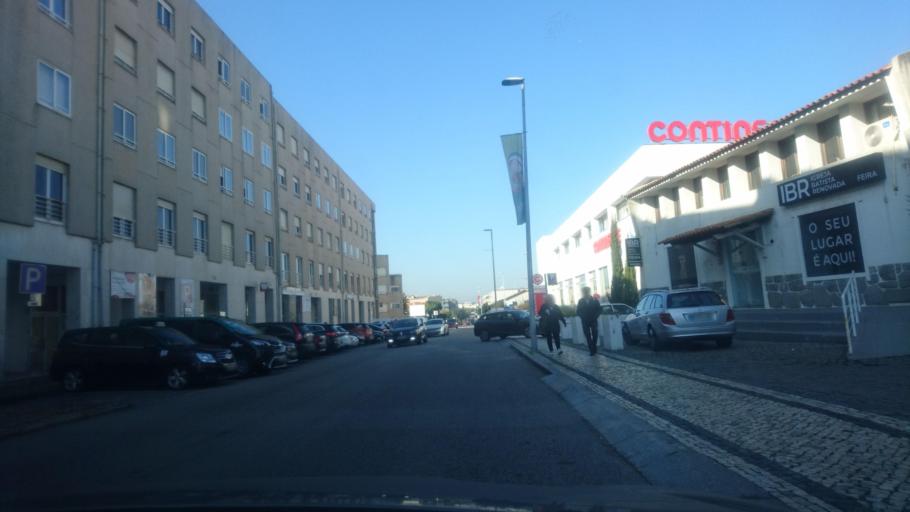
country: PT
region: Aveiro
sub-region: Santa Maria da Feira
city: Feira
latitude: 40.9257
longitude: -8.5481
